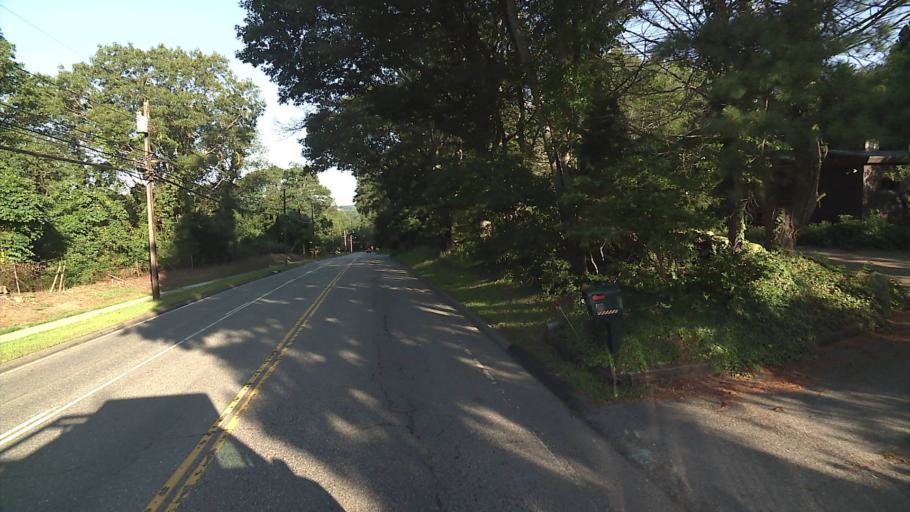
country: US
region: Connecticut
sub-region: New London County
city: Poquonock Bridge
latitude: 41.3461
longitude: -72.0154
